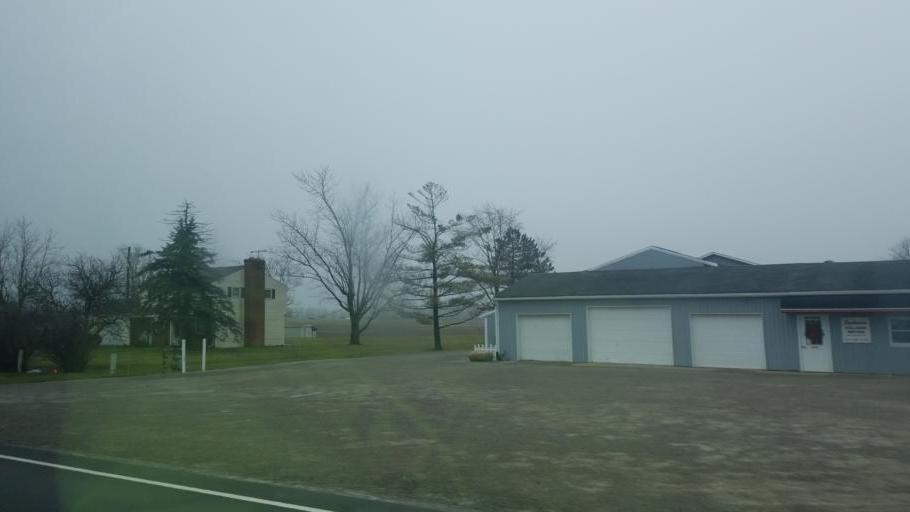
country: US
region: Ohio
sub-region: Union County
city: Marysville
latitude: 40.2568
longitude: -83.4460
